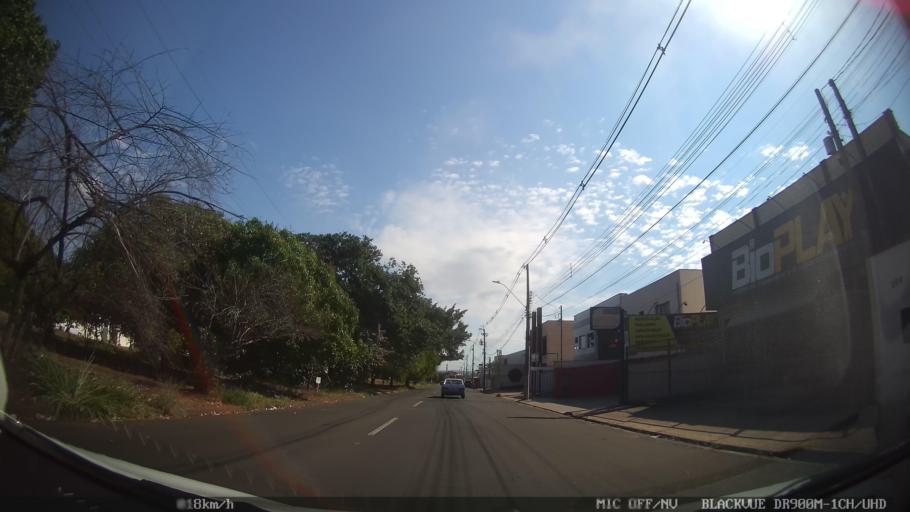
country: BR
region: Sao Paulo
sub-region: Americana
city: Americana
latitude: -22.7193
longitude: -47.3115
